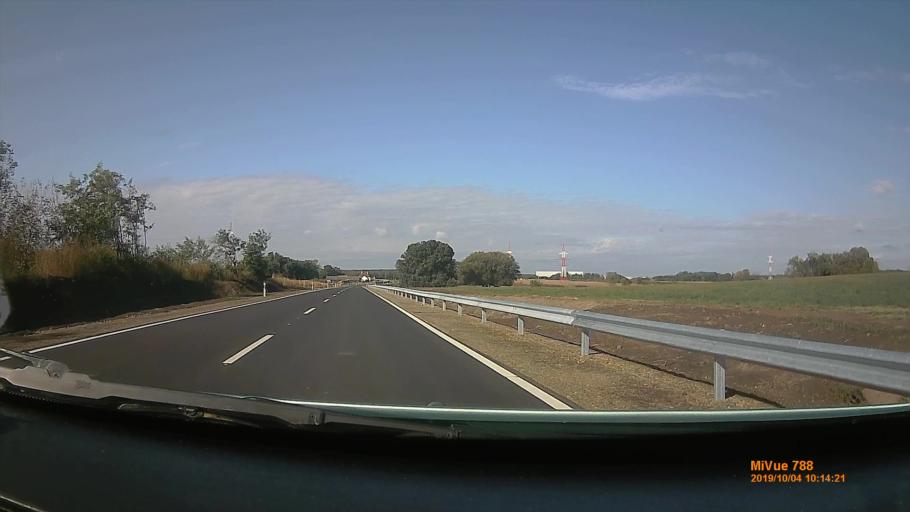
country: HU
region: Szabolcs-Szatmar-Bereg
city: Nyiregyhaza
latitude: 47.9416
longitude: 21.6705
